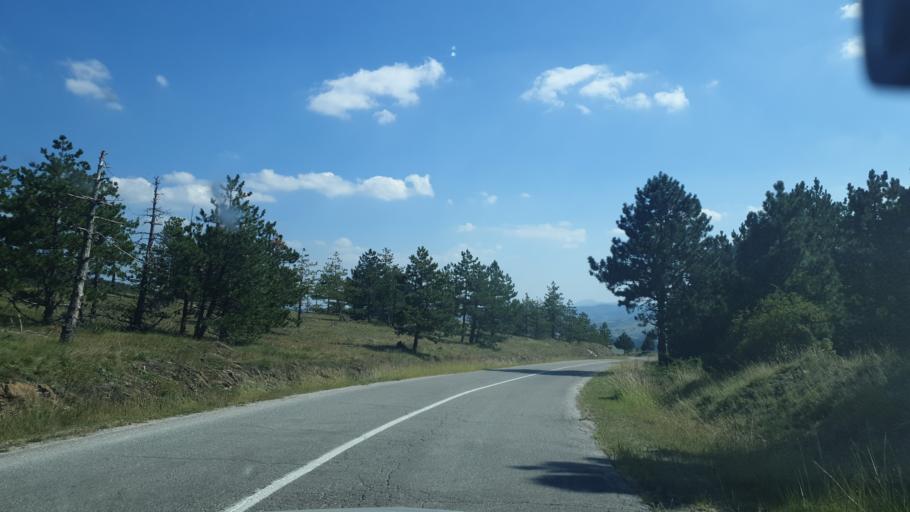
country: RS
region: Central Serbia
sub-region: Zlatiborski Okrug
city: Kosjeric
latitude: 44.0875
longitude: 20.0090
